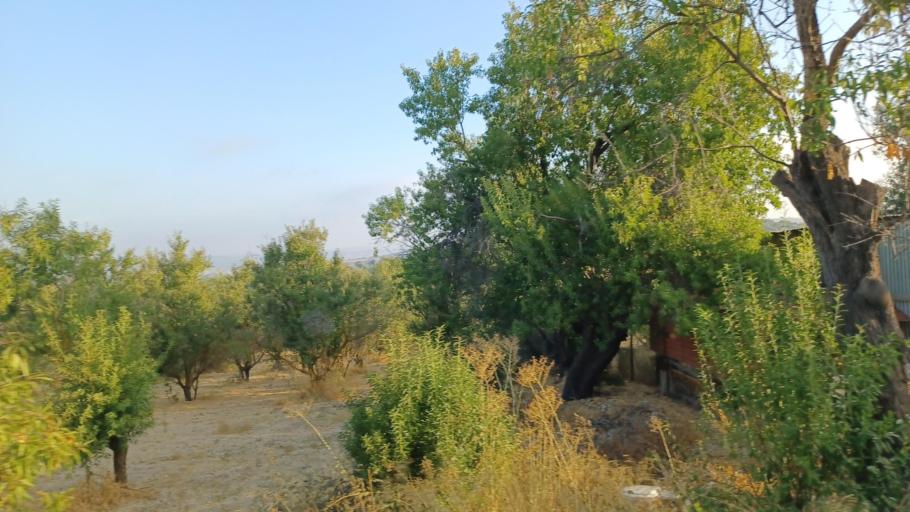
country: CY
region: Pafos
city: Mesogi
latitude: 34.8275
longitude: 32.5783
